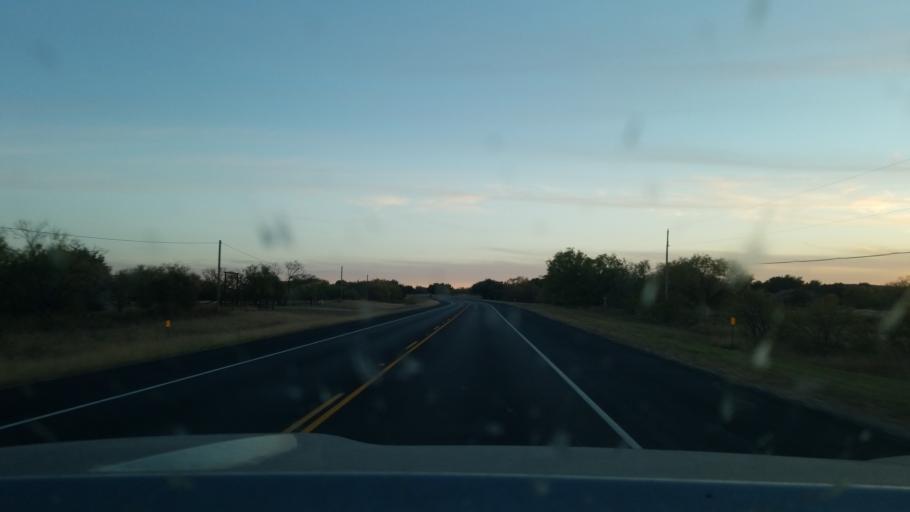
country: US
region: Texas
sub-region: Stephens County
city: Breckenridge
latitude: 32.6249
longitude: -98.9030
